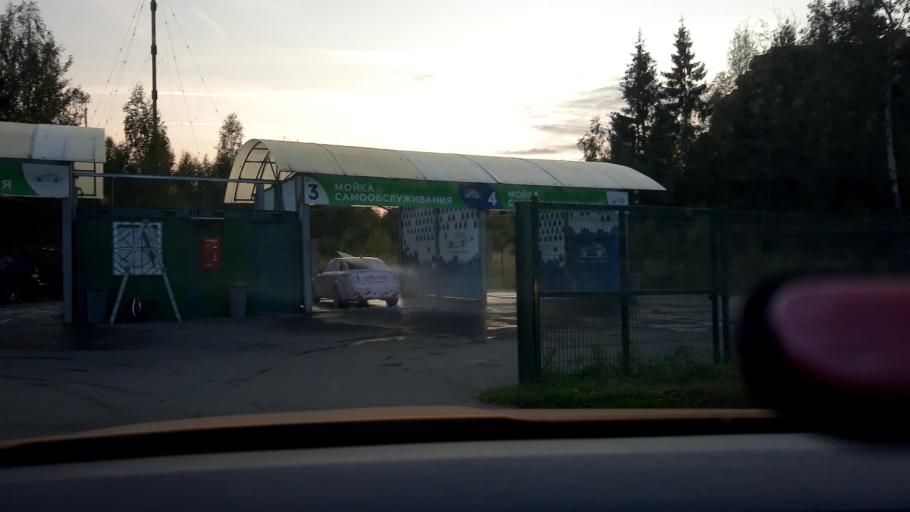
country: RU
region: Moskovskaya
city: Krasnoznamensk
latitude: 55.5903
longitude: 37.0544
